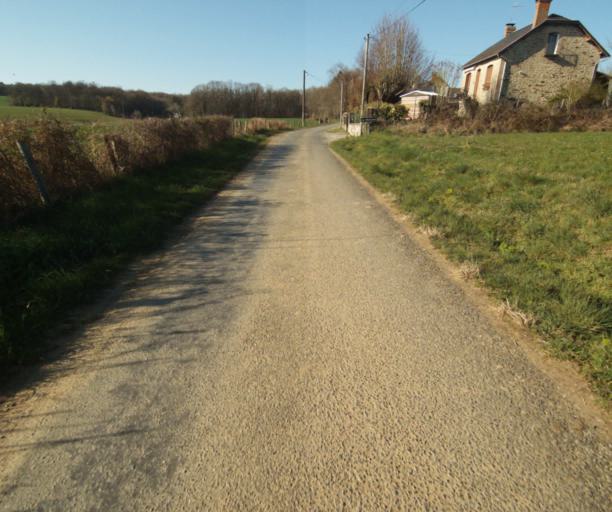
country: FR
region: Limousin
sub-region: Departement de la Correze
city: Chamboulive
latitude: 45.4735
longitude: 1.7244
